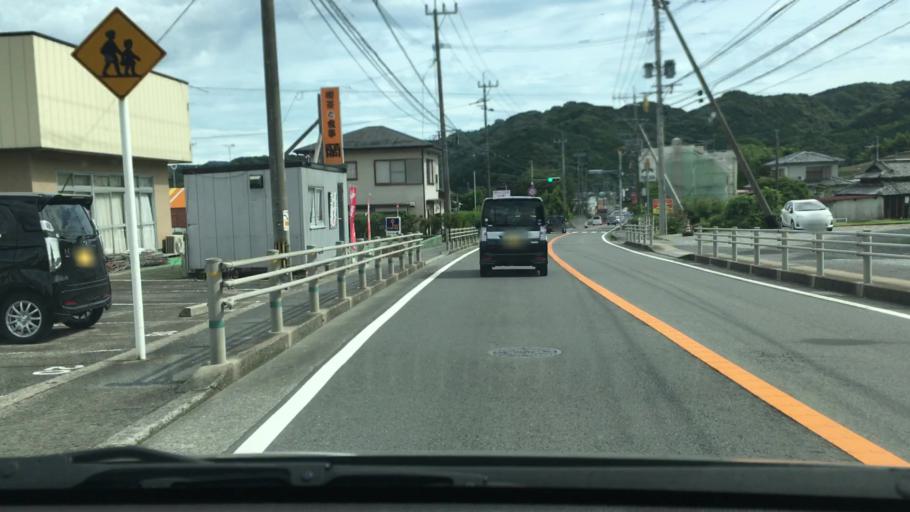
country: JP
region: Nagasaki
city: Togitsu
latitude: 32.8992
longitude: 129.7810
